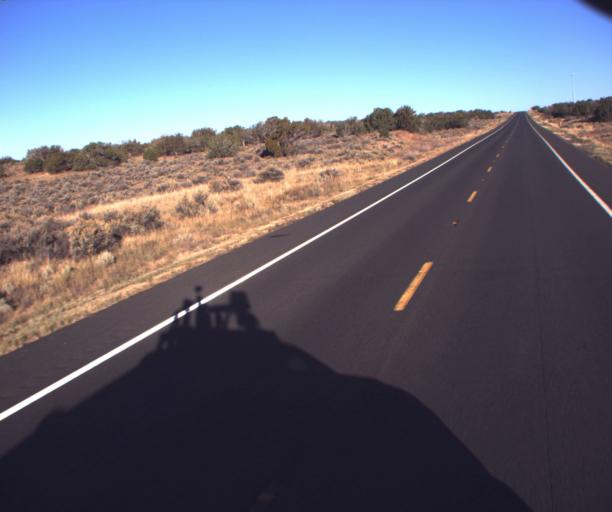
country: US
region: Arizona
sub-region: Apache County
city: Houck
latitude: 35.3394
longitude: -109.4468
